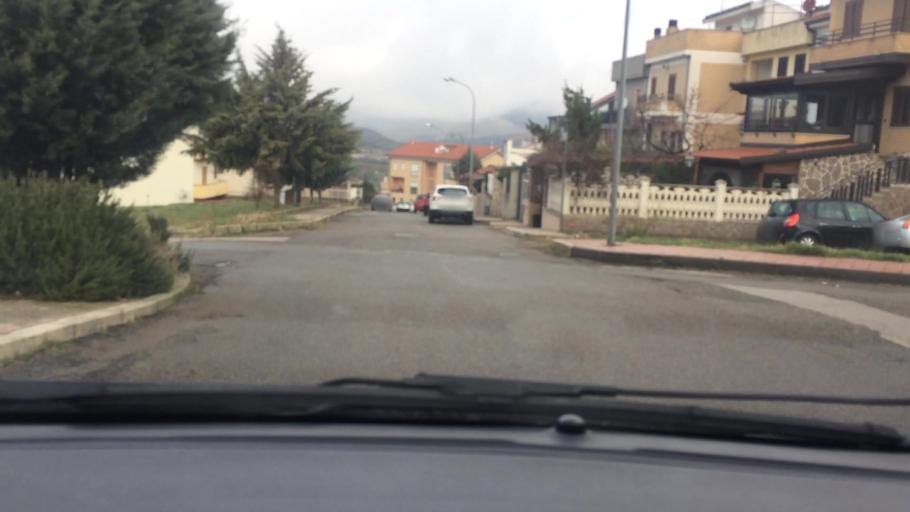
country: IT
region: Basilicate
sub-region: Provincia di Matera
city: San Mauro Forte
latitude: 40.4889
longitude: 16.2434
